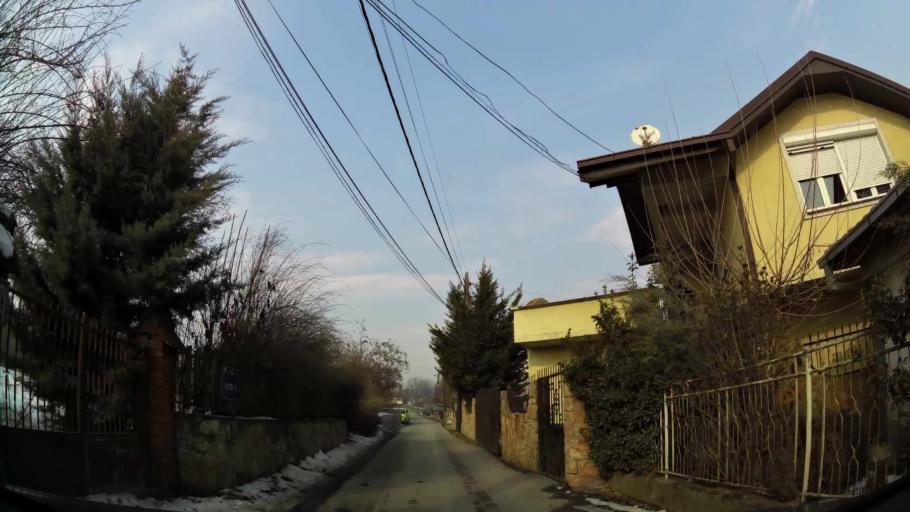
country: MK
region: Karpos
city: Skopje
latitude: 42.0138
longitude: 21.4116
